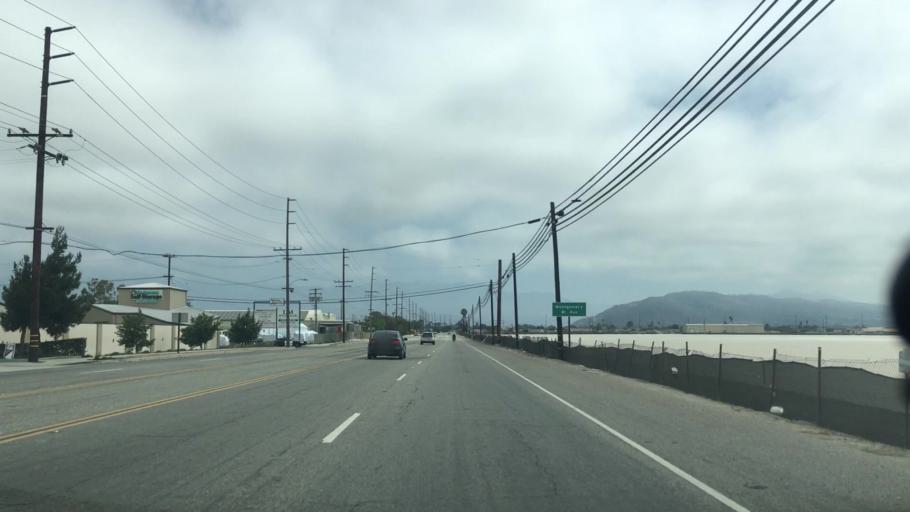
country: US
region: California
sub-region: Ventura County
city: El Rio
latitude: 34.2493
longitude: -119.1600
